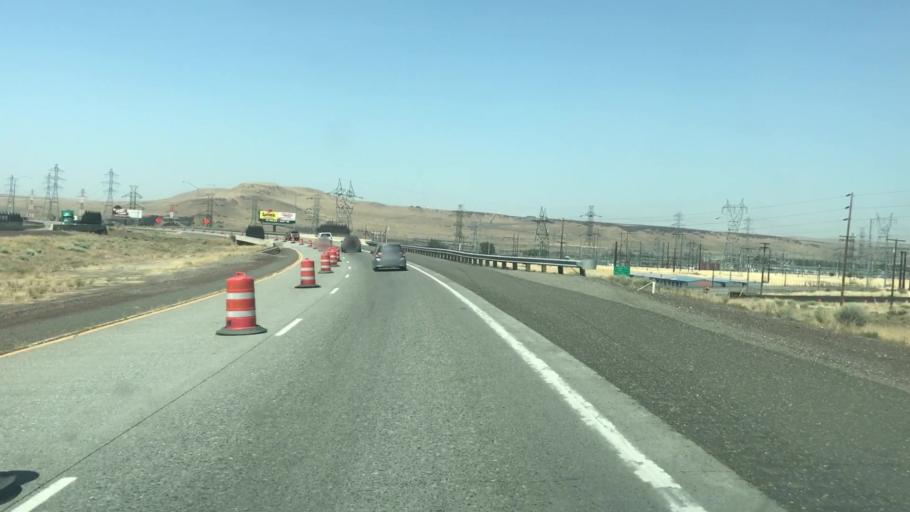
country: US
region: Oregon
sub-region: Umatilla County
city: Umatilla
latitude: 45.9168
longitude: -119.3211
